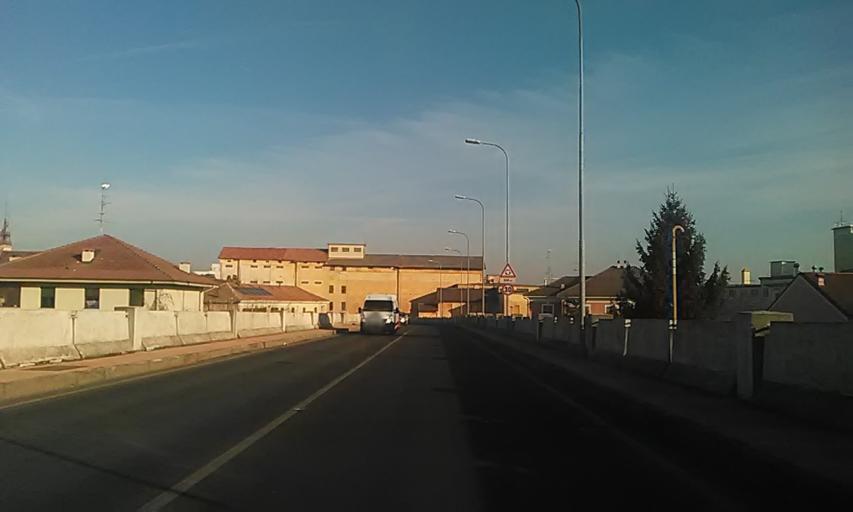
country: IT
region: Piedmont
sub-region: Provincia di Vercelli
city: Vercelli
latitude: 45.3287
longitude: 8.4123
